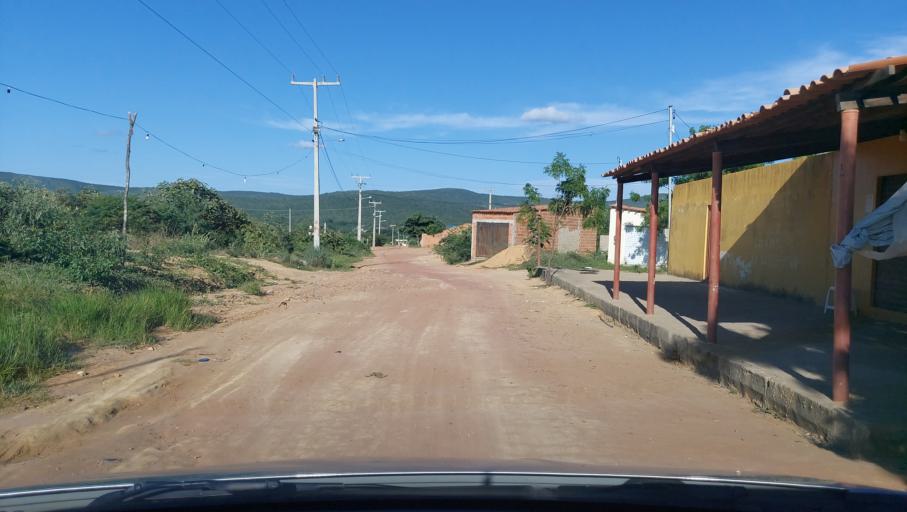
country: BR
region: Bahia
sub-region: Oliveira Dos Brejinhos
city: Beira Rio
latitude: -12.0051
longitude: -42.6337
